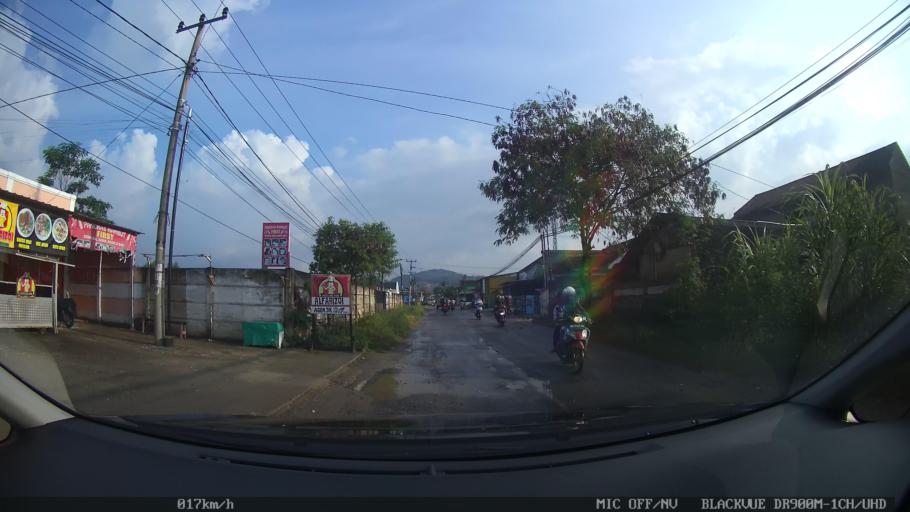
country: ID
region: Lampung
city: Kedaton
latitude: -5.3890
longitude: 105.3155
